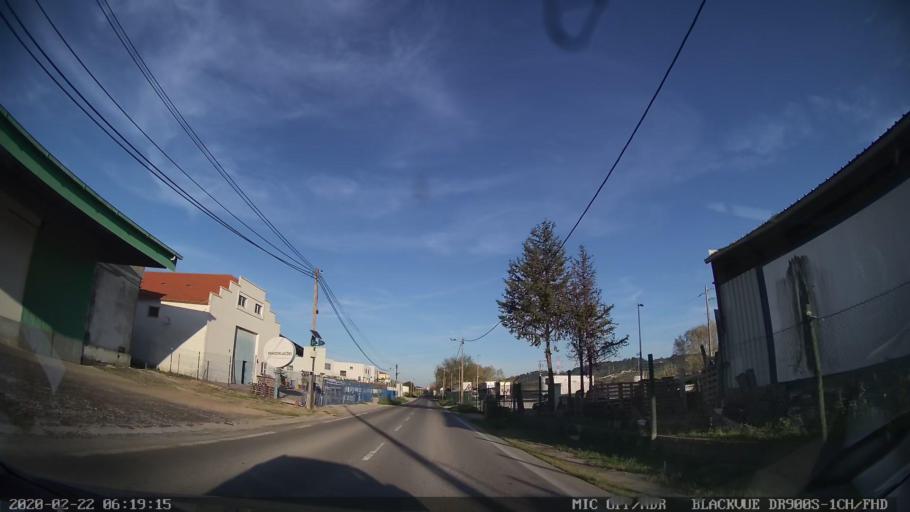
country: PT
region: Lisbon
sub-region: Vila Franca de Xira
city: Castanheira do Ribatejo
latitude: 39.0043
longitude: -9.0006
